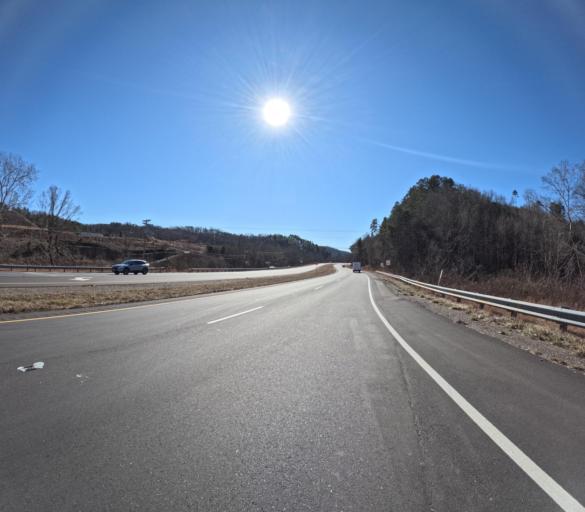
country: US
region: North Carolina
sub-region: Cherokee County
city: Murphy
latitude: 35.1210
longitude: -84.0009
